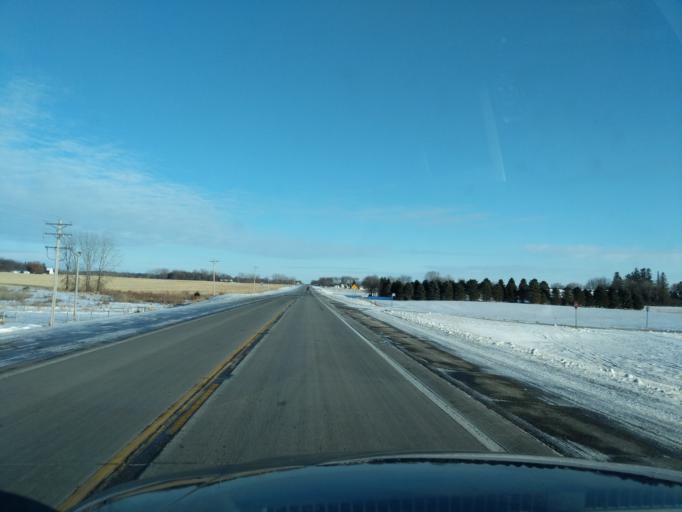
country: US
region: Minnesota
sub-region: McLeod County
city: Hutchinson
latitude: 44.8931
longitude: -94.3156
